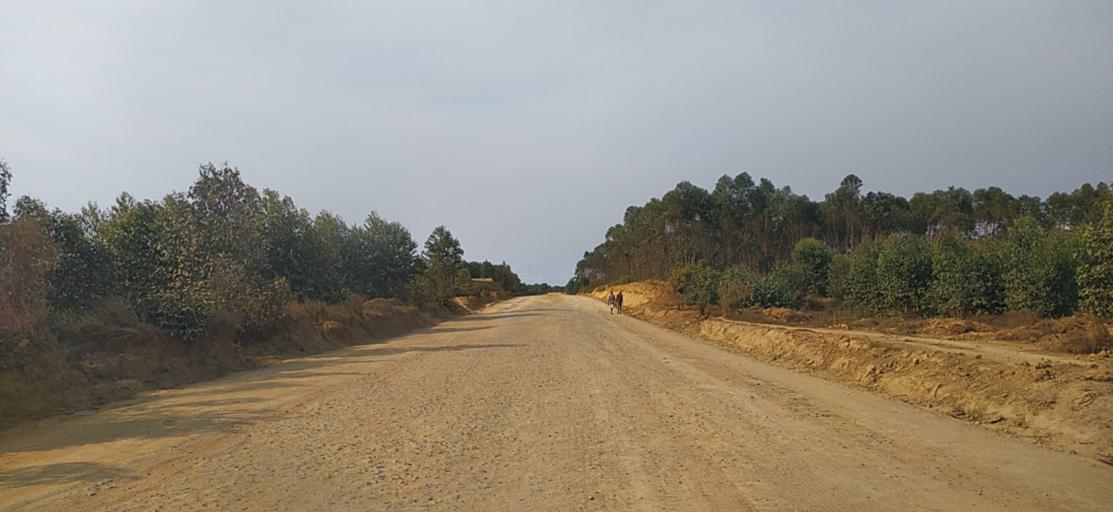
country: MG
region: Alaotra Mangoro
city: Moramanga
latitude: -18.6619
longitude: 48.2737
